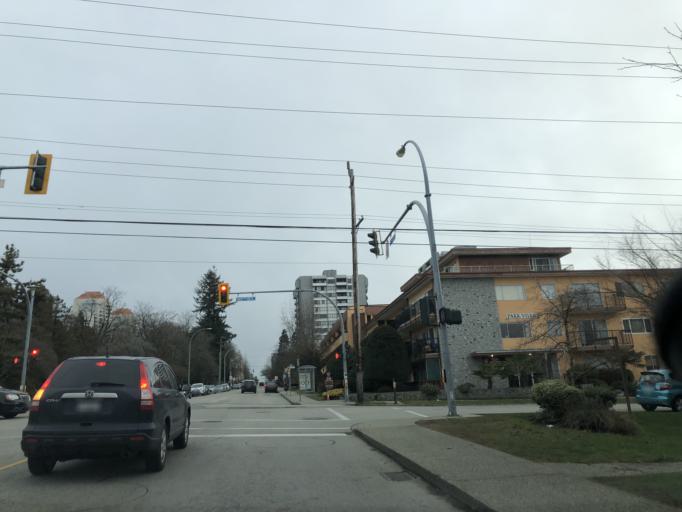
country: CA
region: British Columbia
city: New Westminster
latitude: 49.2094
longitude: -122.9271
